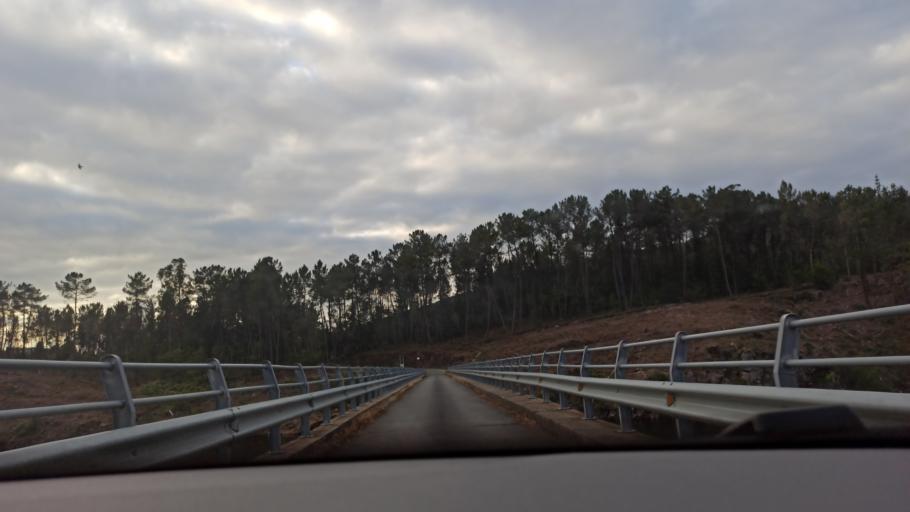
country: ES
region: Galicia
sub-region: Provincia da Coruna
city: Santiso
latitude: 42.8195
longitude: -8.1262
